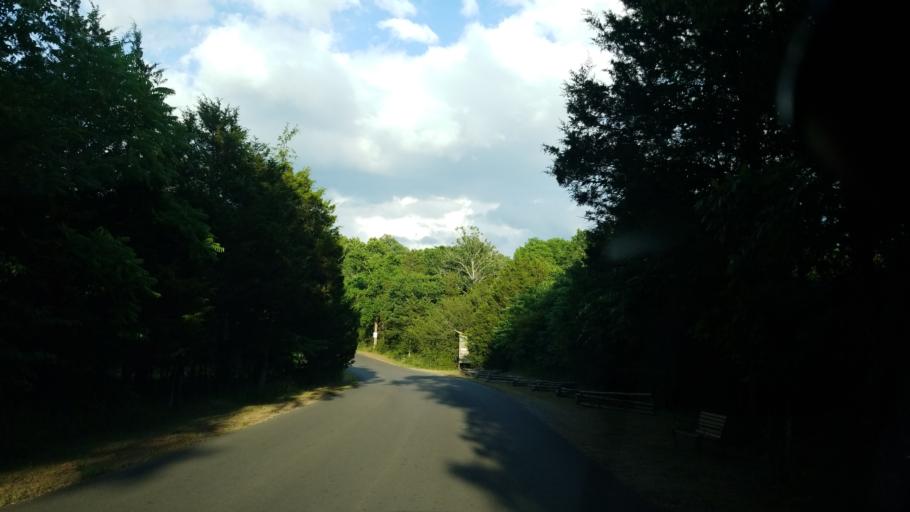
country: US
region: Tennessee
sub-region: Rutherford County
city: La Vergne
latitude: 36.0850
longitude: -86.5940
